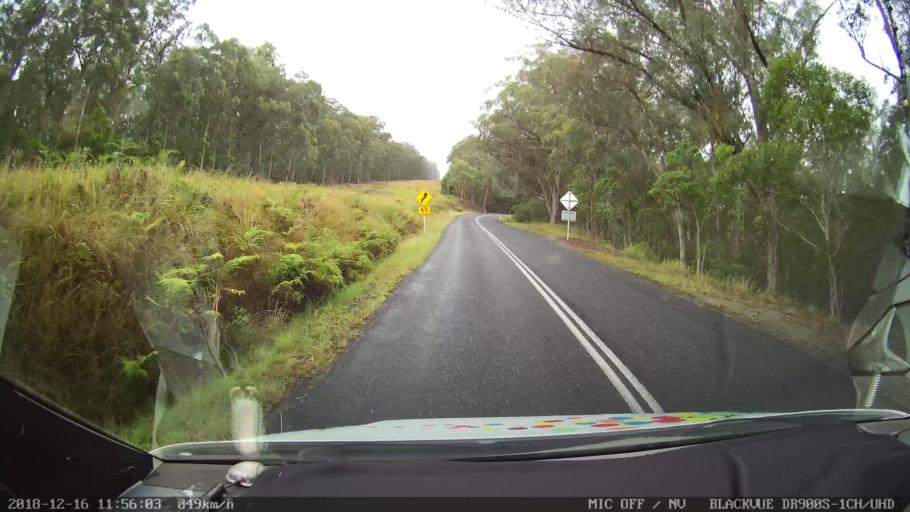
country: AU
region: New South Wales
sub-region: Tenterfield Municipality
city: Carrolls Creek
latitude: -28.9161
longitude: 152.2949
